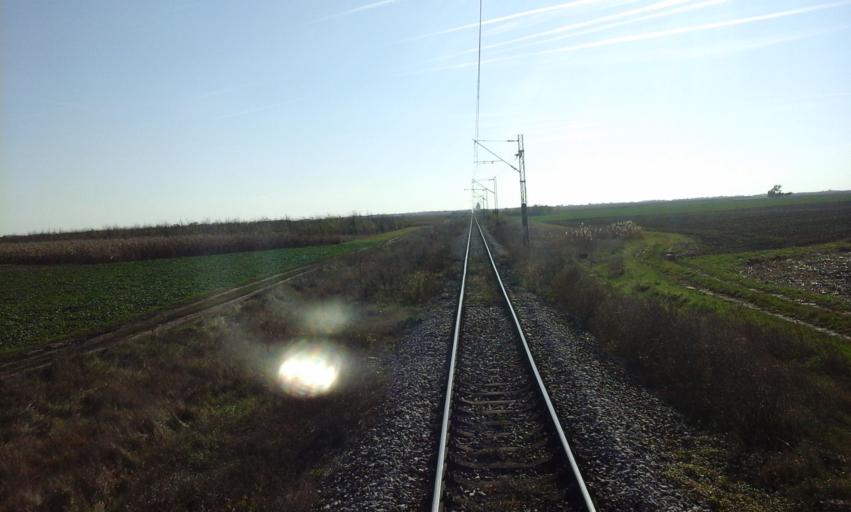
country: RS
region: Autonomna Pokrajina Vojvodina
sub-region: Severnobacki Okrug
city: Subotica
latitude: 45.9823
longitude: 19.6748
